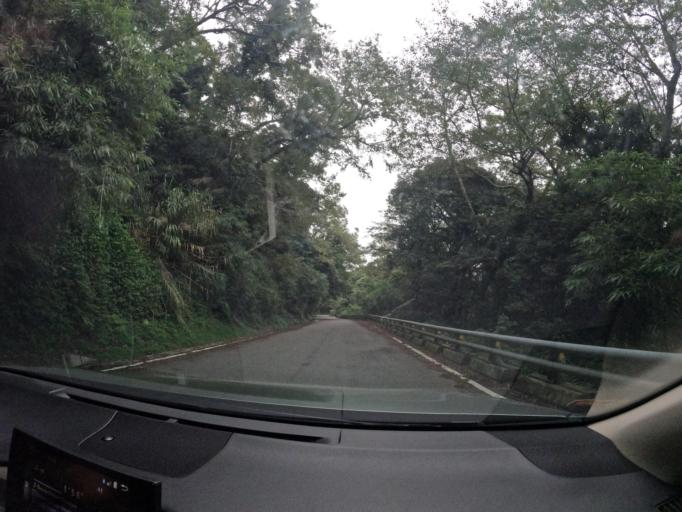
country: TW
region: Taiwan
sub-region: Taitung
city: Taitung
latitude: 23.2421
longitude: 120.9906
